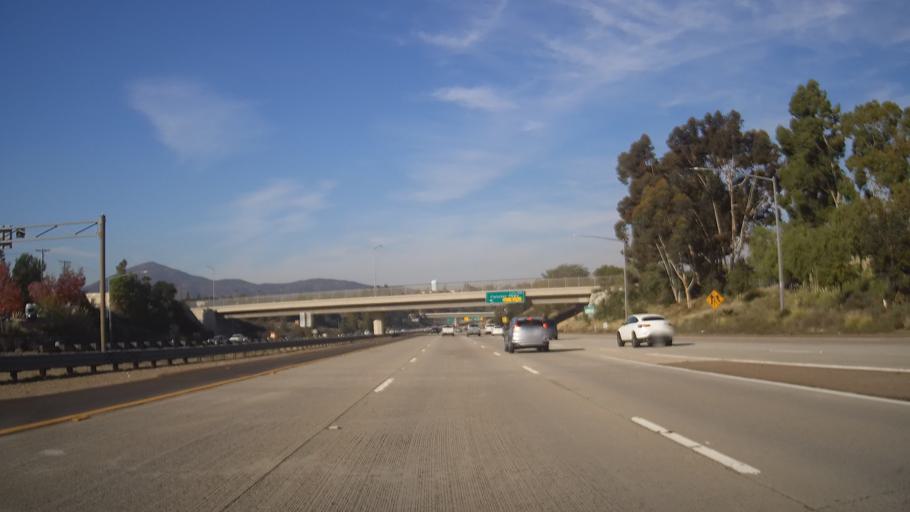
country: US
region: California
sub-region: San Diego County
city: La Mesa
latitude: 32.7809
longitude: -117.0045
